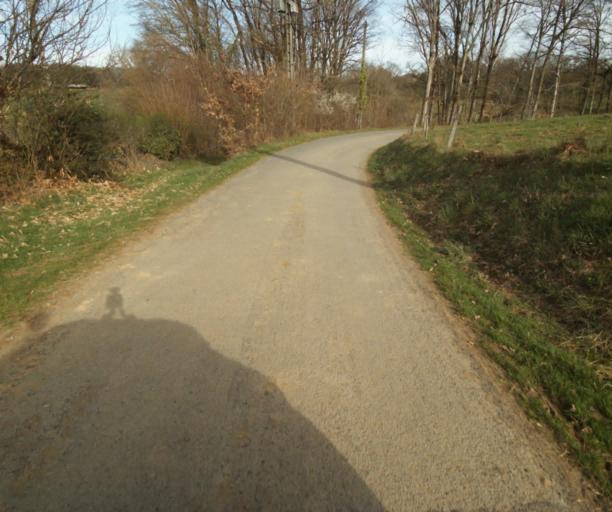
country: FR
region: Limousin
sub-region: Departement de la Correze
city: Chamboulive
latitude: 45.4219
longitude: 1.7614
